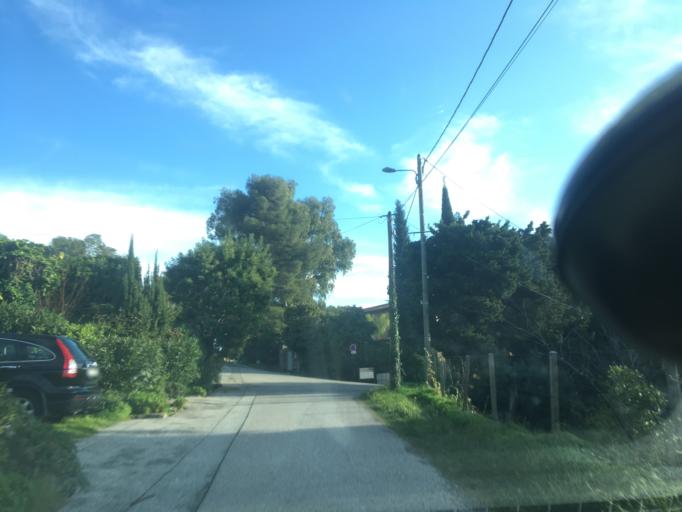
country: FR
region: Provence-Alpes-Cote d'Azur
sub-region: Departement du Var
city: Cavalaire-sur-Mer
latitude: 43.1579
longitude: 6.4768
